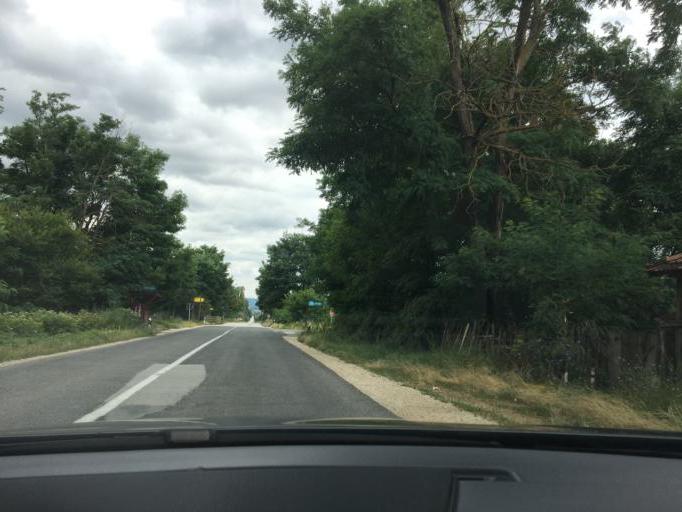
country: MK
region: Opstina Rankovce
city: Rankovce
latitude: 42.1701
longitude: 22.1605
